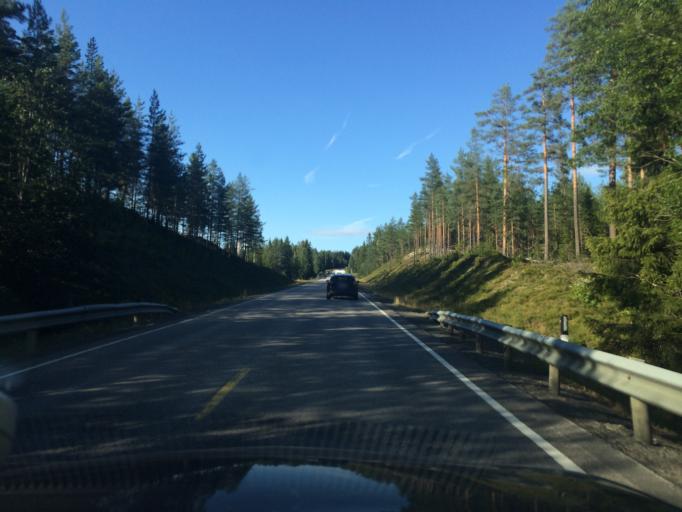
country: NO
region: Hedmark
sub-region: Elverum
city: Elverum
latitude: 60.9521
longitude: 11.7000
